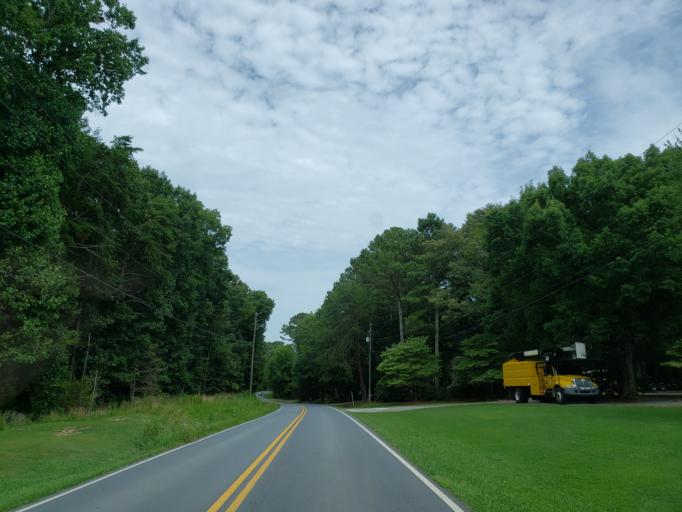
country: US
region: Georgia
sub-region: Pickens County
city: Jasper
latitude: 34.4461
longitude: -84.4161
